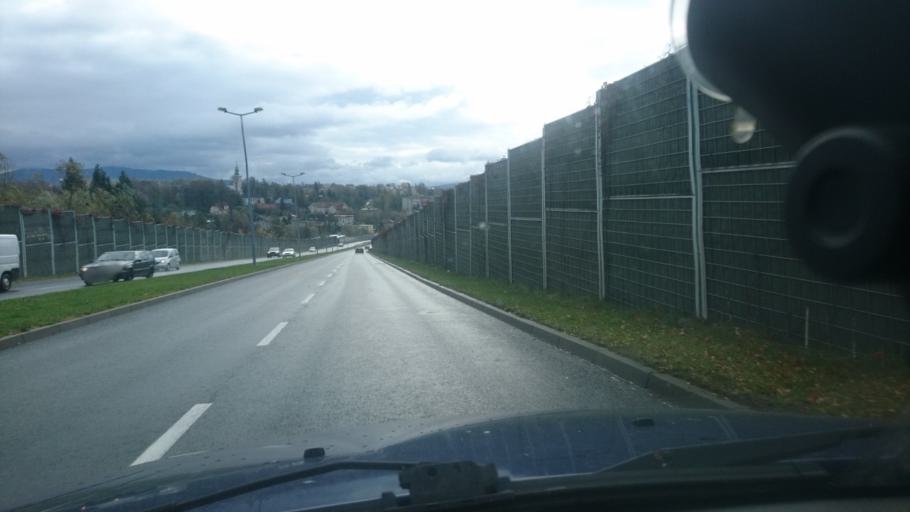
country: PL
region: Silesian Voivodeship
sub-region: Bielsko-Biala
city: Bielsko-Biala
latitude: 49.8277
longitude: 19.0135
